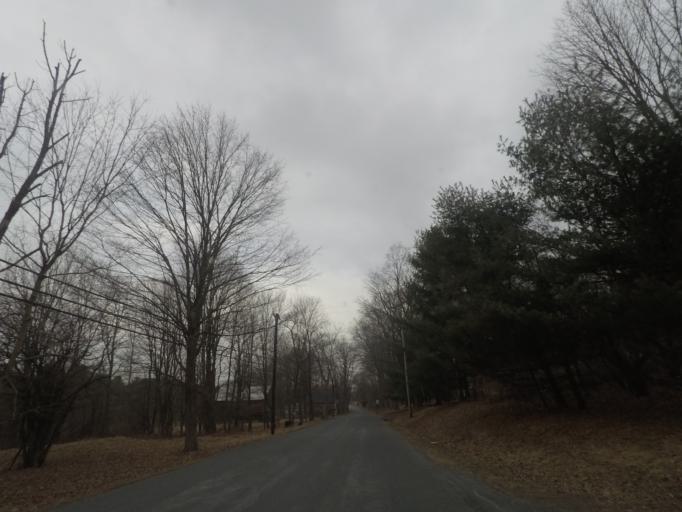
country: US
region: New York
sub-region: Rensselaer County
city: East Greenbush
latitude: 42.5751
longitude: -73.6696
